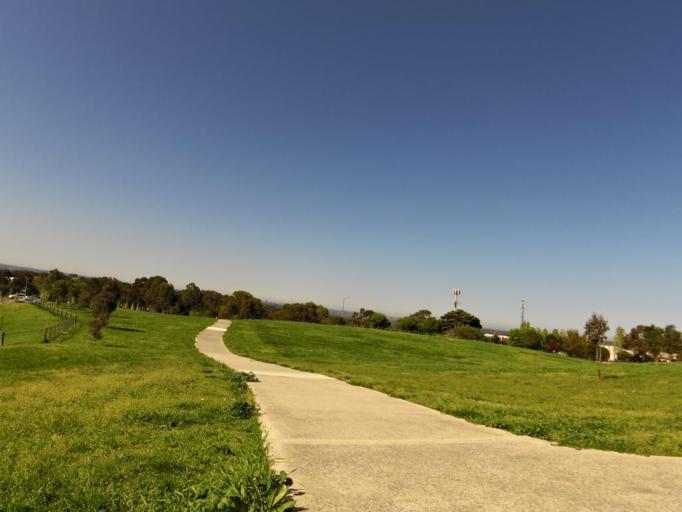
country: AU
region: Victoria
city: Plenty
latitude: -37.6856
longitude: 145.1142
